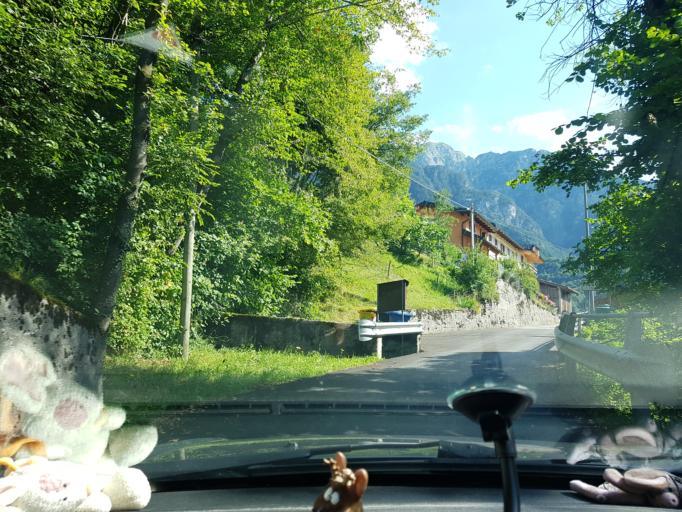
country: IT
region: Friuli Venezia Giulia
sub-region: Provincia di Udine
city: Dogna
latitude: 46.4457
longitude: 13.3116
